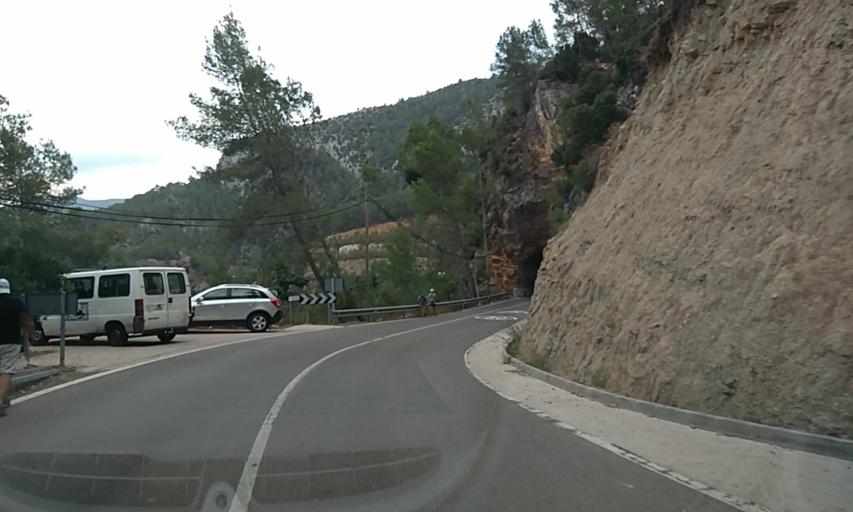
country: ES
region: Valencia
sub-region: Provincia de Castello
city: Montanejos
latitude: 40.0769
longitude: -0.5394
